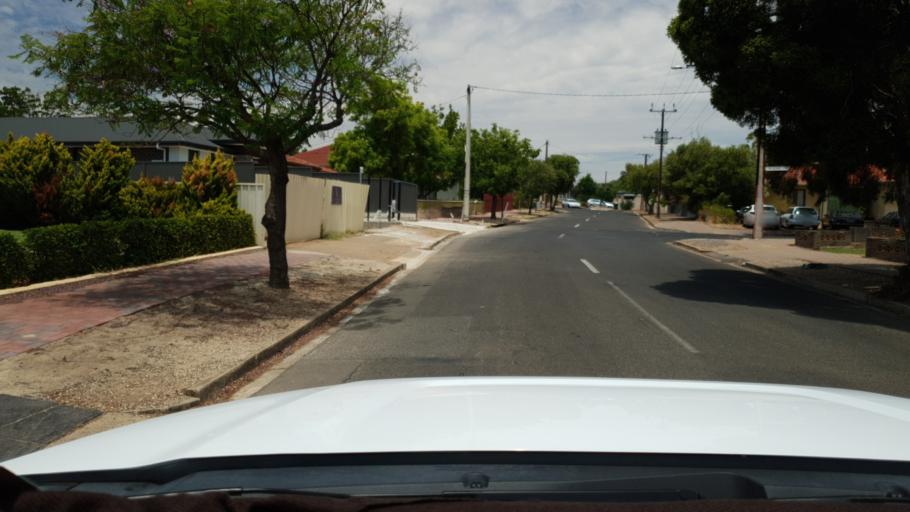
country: AU
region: South Australia
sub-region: Marion
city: Clovelly Park
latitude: -35.0024
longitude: 138.5824
